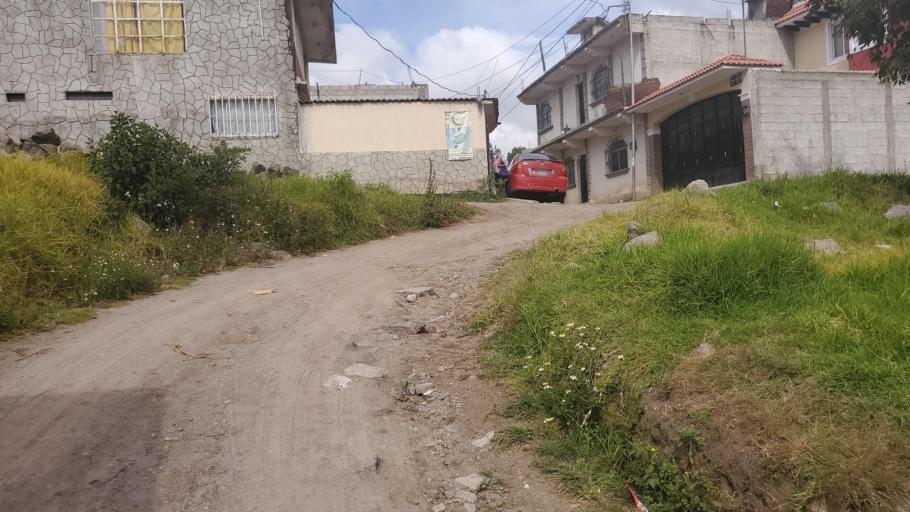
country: GT
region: Quetzaltenango
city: Quetzaltenango
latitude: 14.8367
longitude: -91.5434
